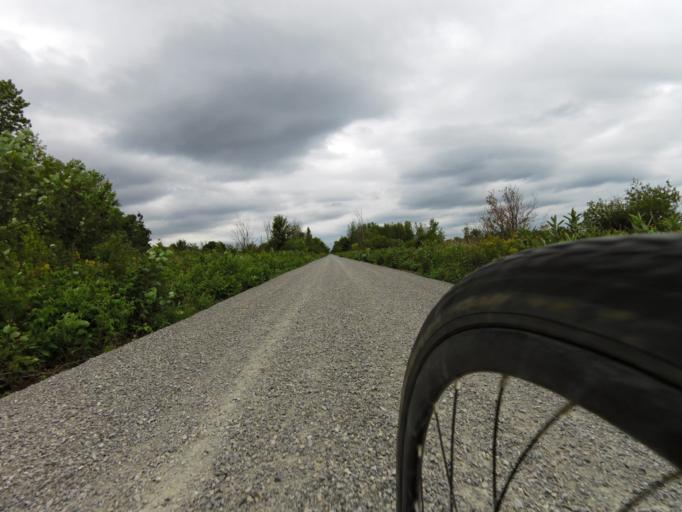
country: CA
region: Ontario
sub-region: Lanark County
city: Smiths Falls
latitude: 44.9266
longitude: -76.0323
